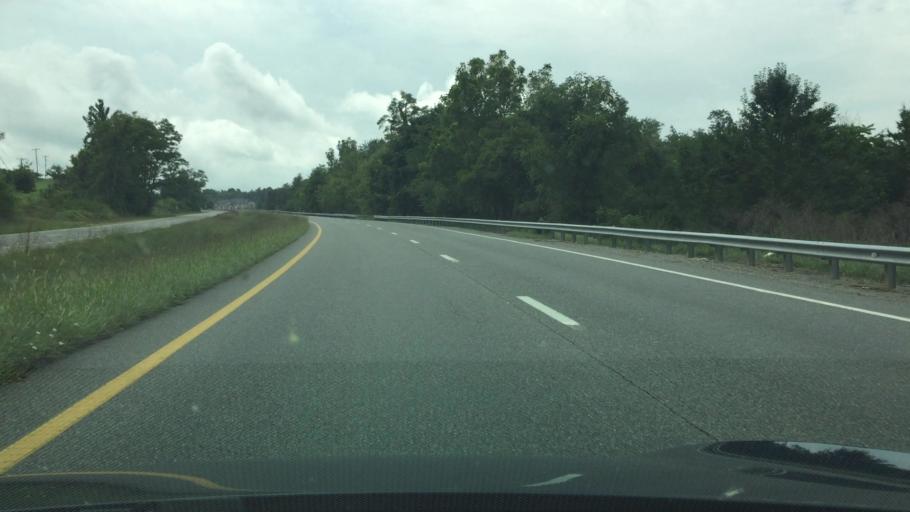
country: US
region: Virginia
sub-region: City of Radford
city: Radford
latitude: 37.1061
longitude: -80.5202
